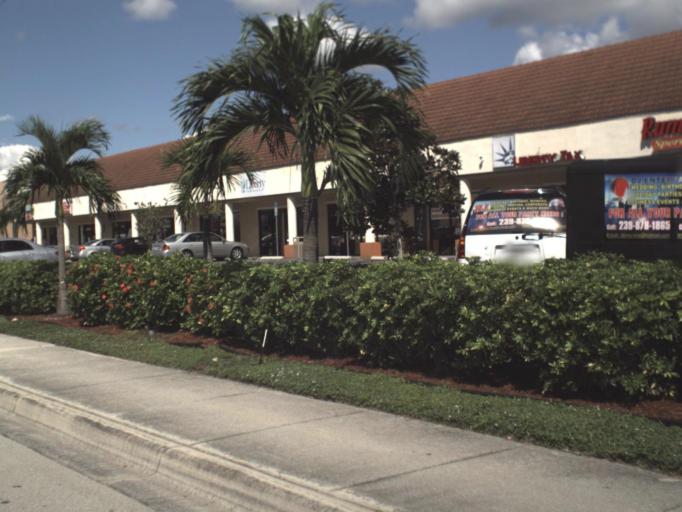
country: US
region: Florida
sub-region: Lee County
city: Lochmoor Waterway Estates
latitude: 26.6576
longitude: -81.9410
